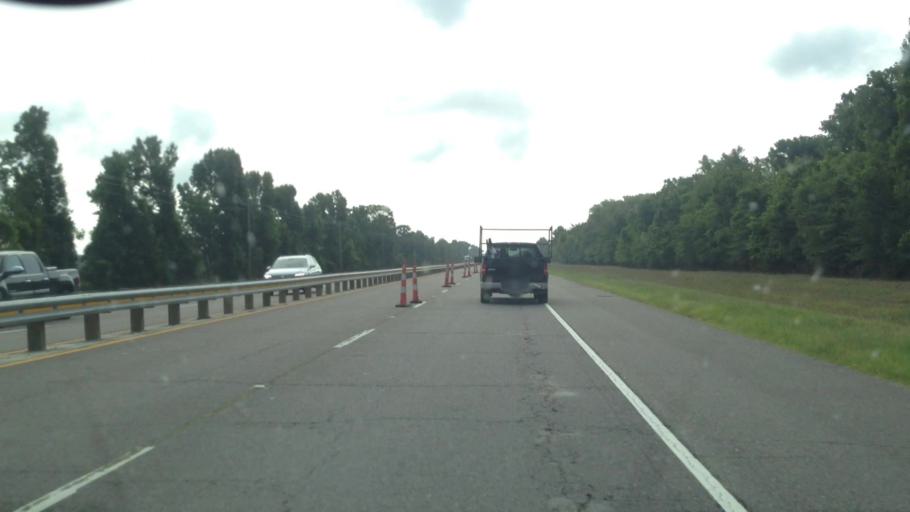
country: US
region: Louisiana
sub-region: Pointe Coupee Parish
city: Livonia
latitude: 30.5536
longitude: -91.5140
